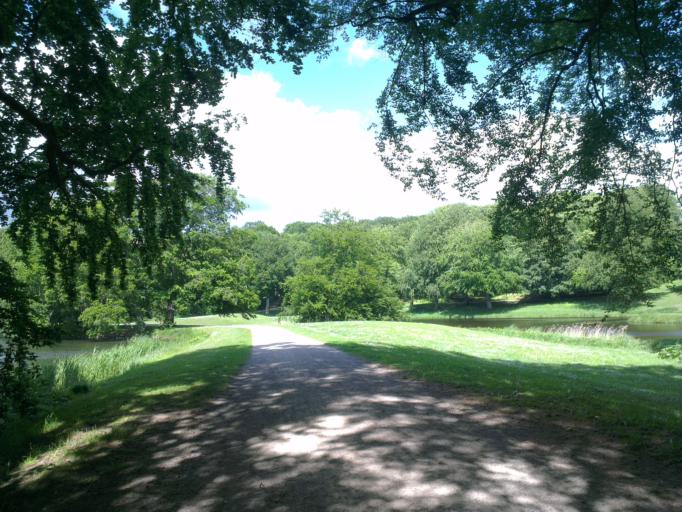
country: DK
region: Capital Region
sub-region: Hillerod Kommune
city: Hillerod
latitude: 55.9398
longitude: 12.3012
